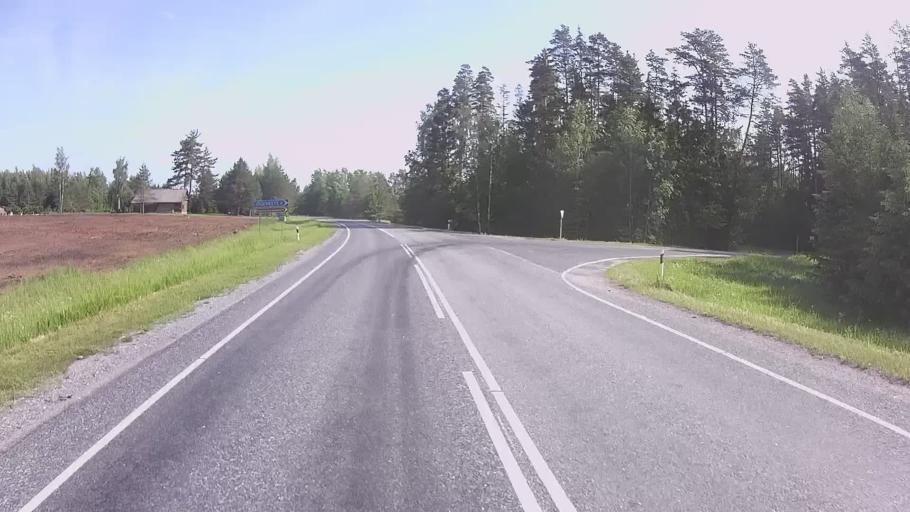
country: EE
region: Valgamaa
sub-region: Torva linn
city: Torva
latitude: 58.0332
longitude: 25.9706
